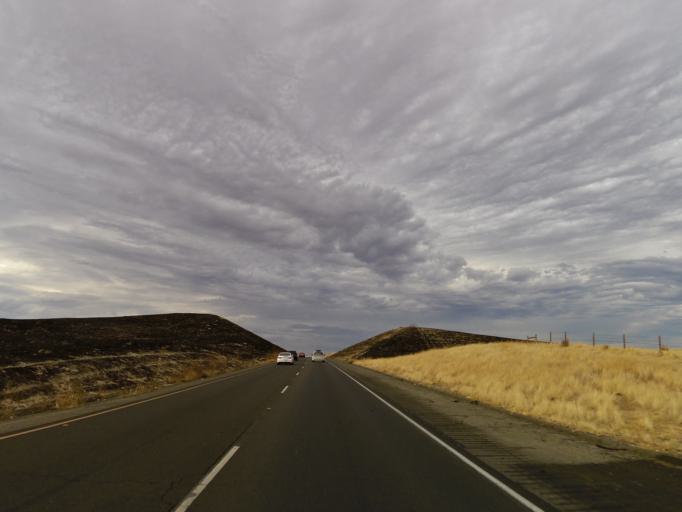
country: US
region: California
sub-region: Fresno County
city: Coalinga
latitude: 36.3196
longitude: -120.2895
